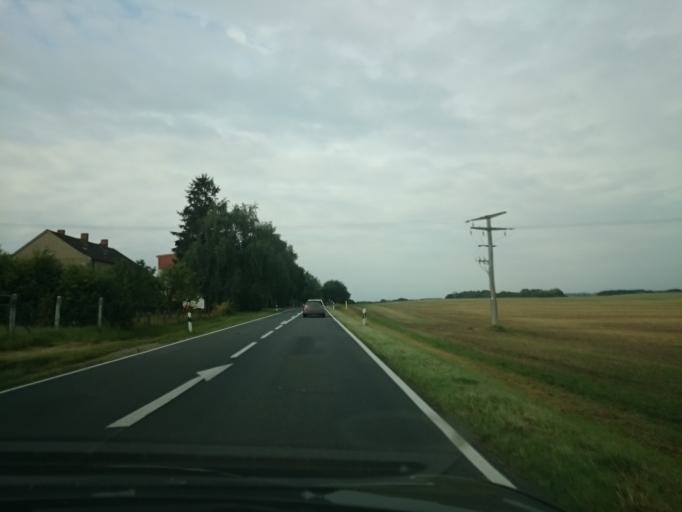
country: DE
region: Mecklenburg-Vorpommern
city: Mollenhagen
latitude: 53.5490
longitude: 12.8495
